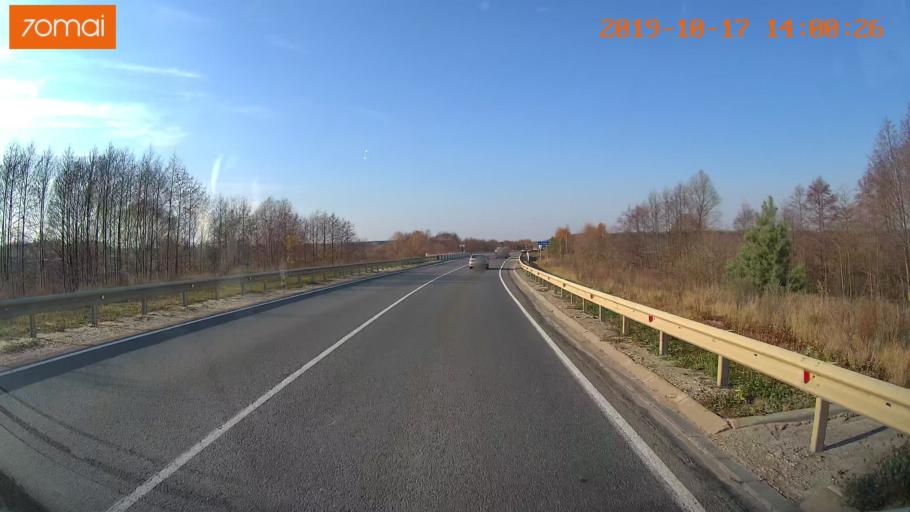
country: RU
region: Rjazan
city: Spas-Klepiki
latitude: 55.1455
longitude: 40.1803
